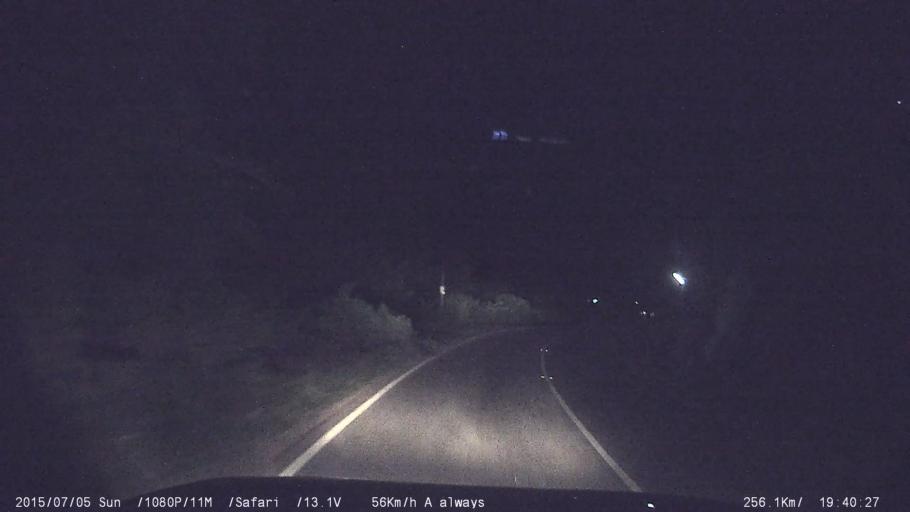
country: IN
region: Kerala
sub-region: Palakkad district
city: Palakkad
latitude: 10.7519
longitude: 76.5599
